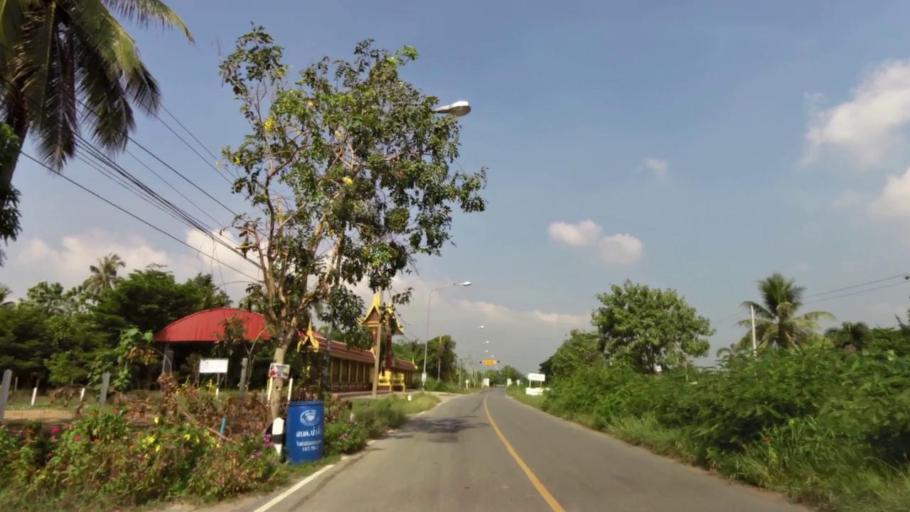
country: TH
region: Ang Thong
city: Ang Thong
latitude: 14.6007
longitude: 100.3991
